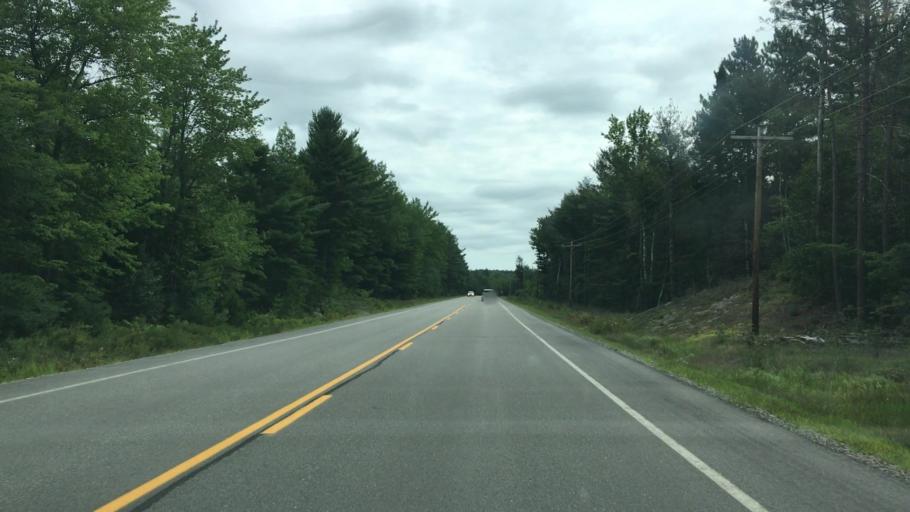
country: US
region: Maine
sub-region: Washington County
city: Machias
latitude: 45.0011
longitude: -67.5781
